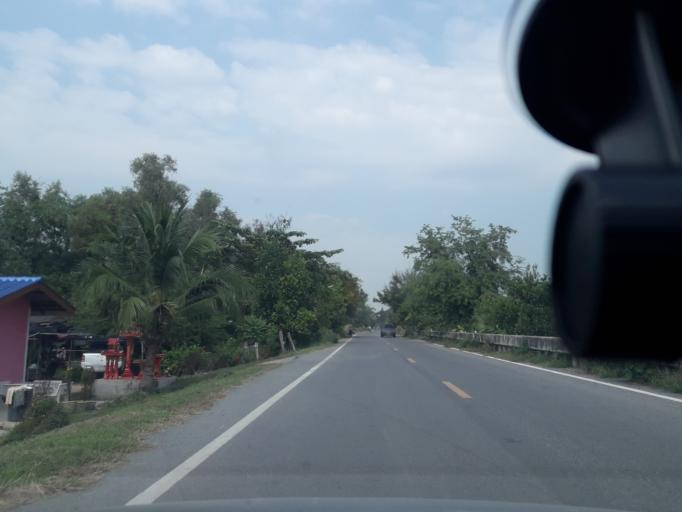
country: TH
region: Sara Buri
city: Nong Khae
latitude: 14.2324
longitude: 100.8914
